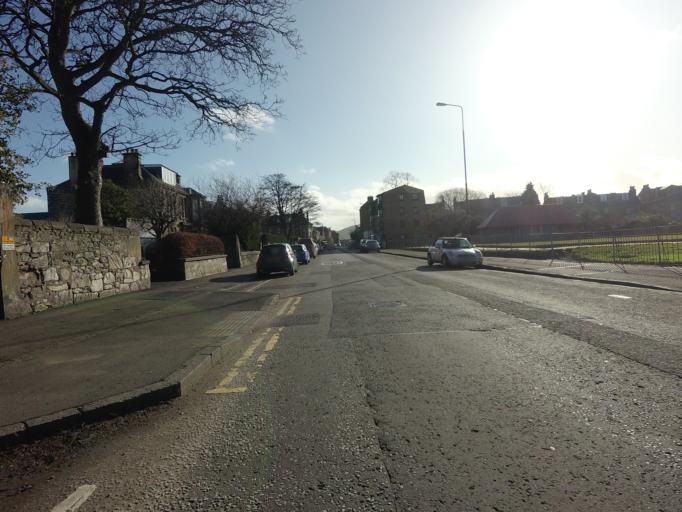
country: GB
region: Scotland
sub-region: Edinburgh
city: Edinburgh
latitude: 55.9750
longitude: -3.1903
